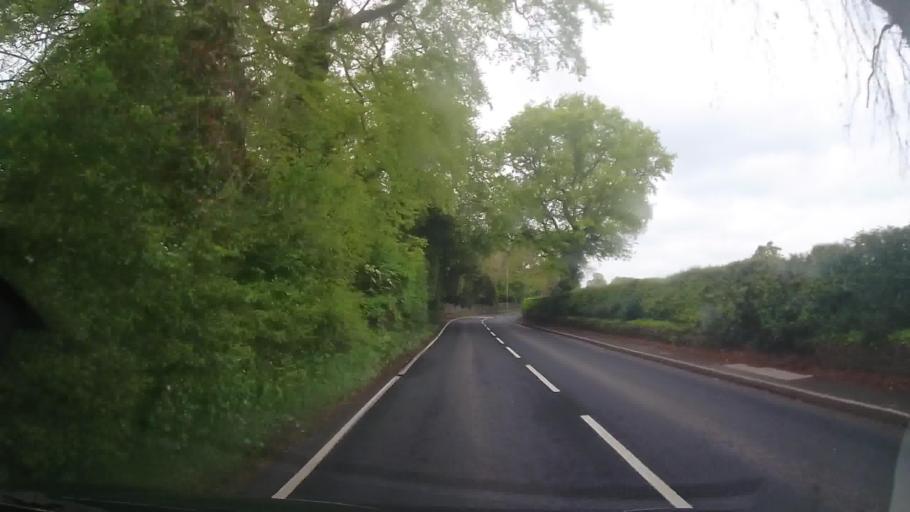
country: GB
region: Wales
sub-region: Wrexham
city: Overton
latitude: 52.9706
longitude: -2.9412
